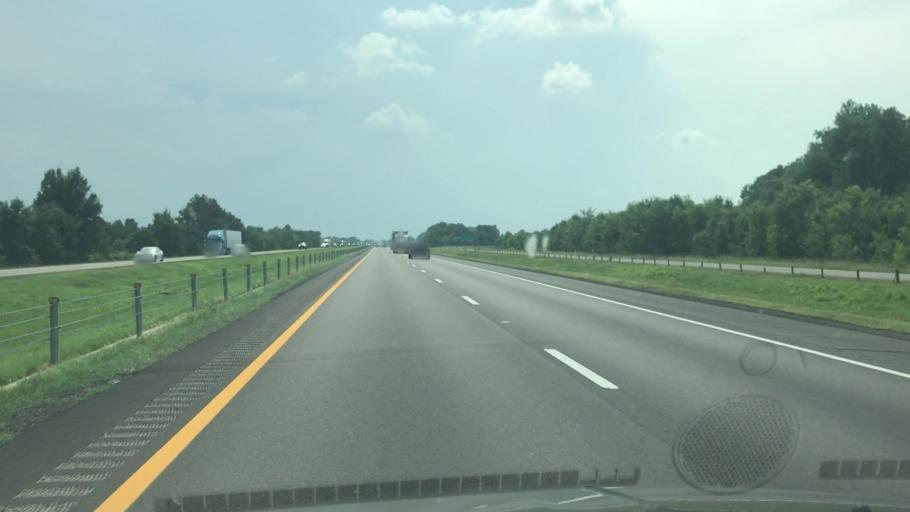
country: US
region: Arkansas
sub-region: Crittenden County
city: Earle
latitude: 35.1461
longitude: -90.4131
